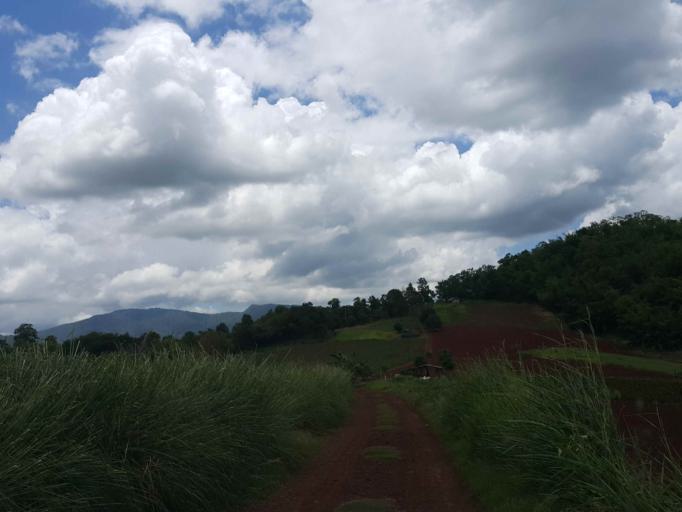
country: TH
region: Chiang Mai
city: Samoeng
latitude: 18.7757
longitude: 98.8240
